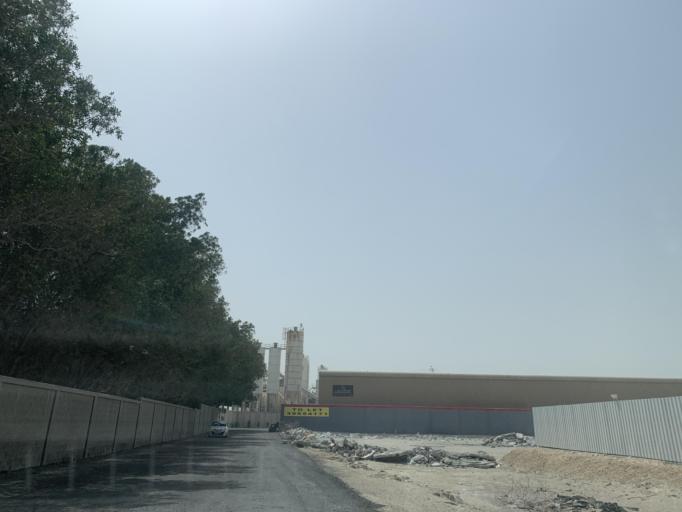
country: BH
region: Northern
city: Madinat `Isa
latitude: 26.1885
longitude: 50.5300
